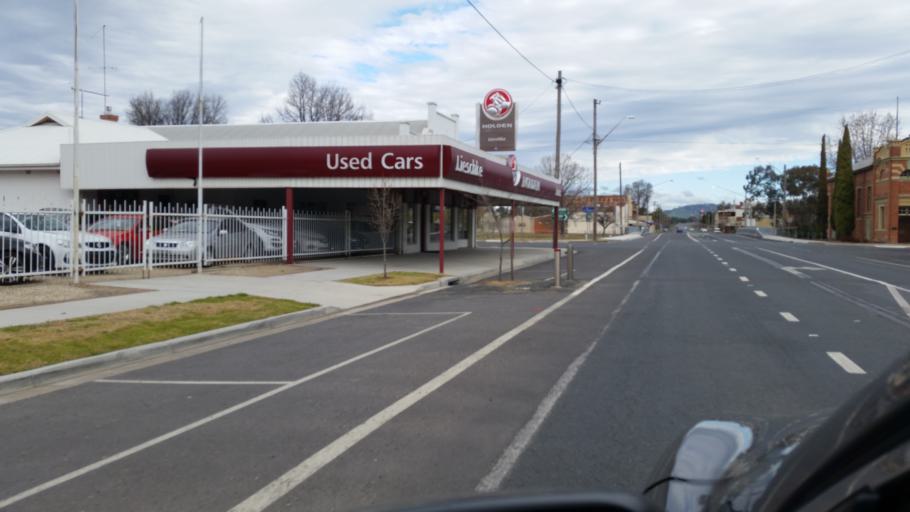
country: AU
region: New South Wales
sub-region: Greater Hume Shire
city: Holbrook
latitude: -35.7247
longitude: 147.3133
